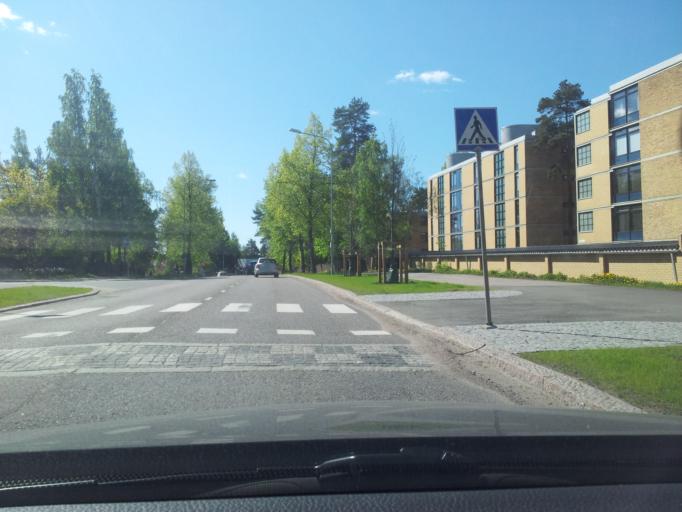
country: FI
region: Uusimaa
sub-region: Helsinki
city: Kauniainen
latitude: 60.1747
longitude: 24.7291
